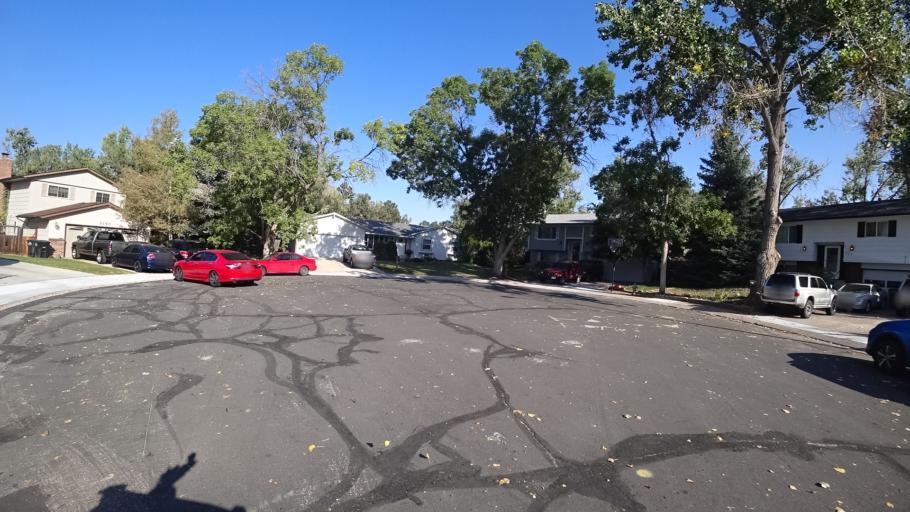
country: US
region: Colorado
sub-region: El Paso County
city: Cimarron Hills
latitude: 38.8769
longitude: -104.7424
